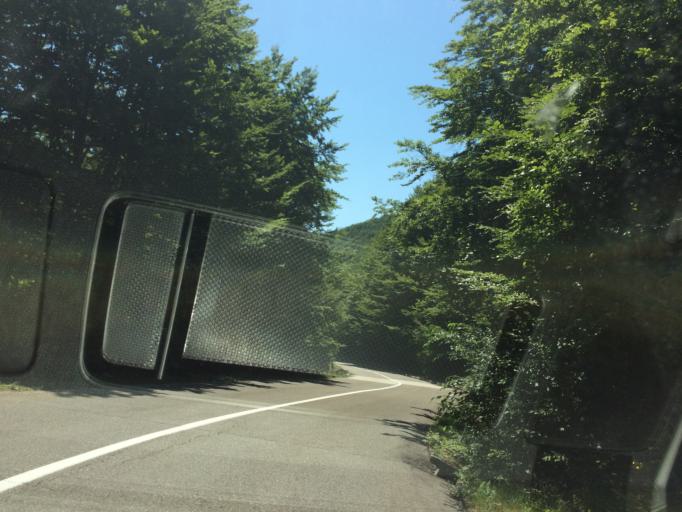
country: ME
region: Opstina Savnik
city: Savnik
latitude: 42.9490
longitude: 19.0940
